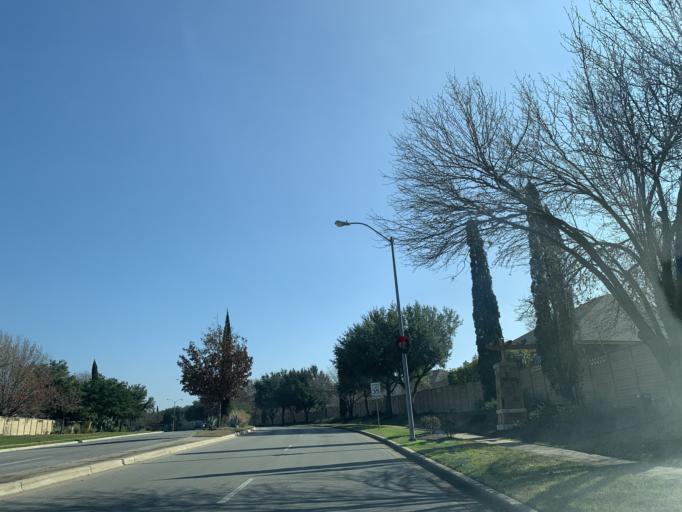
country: US
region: Texas
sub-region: Williamson County
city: Round Rock
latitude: 30.5078
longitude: -97.6271
